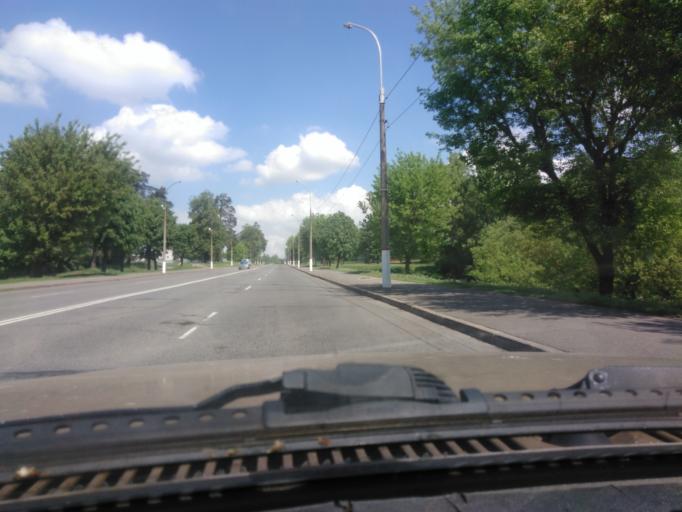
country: BY
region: Mogilev
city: Mahilyow
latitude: 53.9238
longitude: 30.3120
